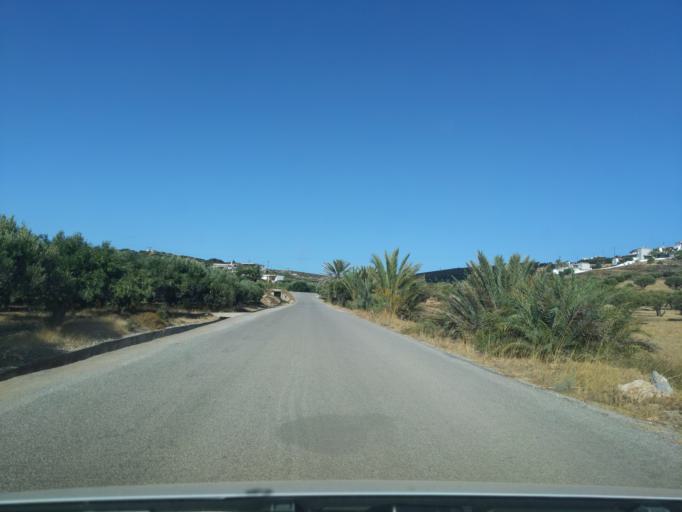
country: GR
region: Crete
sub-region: Nomos Lasithiou
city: Palekastro
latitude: 35.2157
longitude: 26.2662
